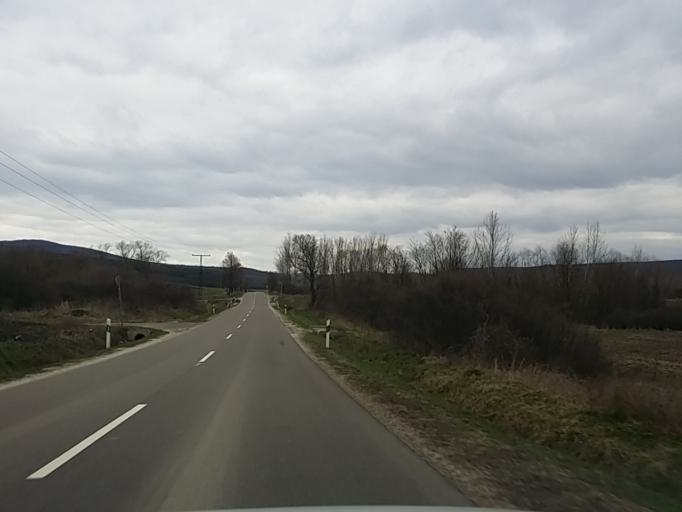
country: HU
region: Heves
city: Verpelet
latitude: 47.8652
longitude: 20.2018
